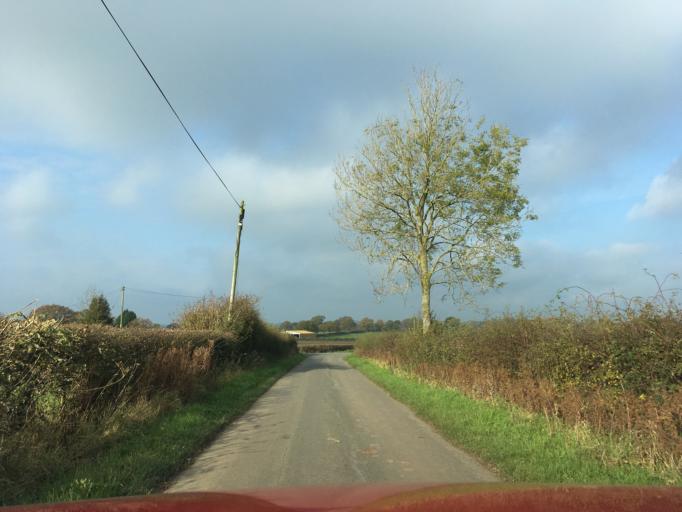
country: GB
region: England
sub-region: South Gloucestershire
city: Wickwar
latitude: 51.5750
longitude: -2.4297
